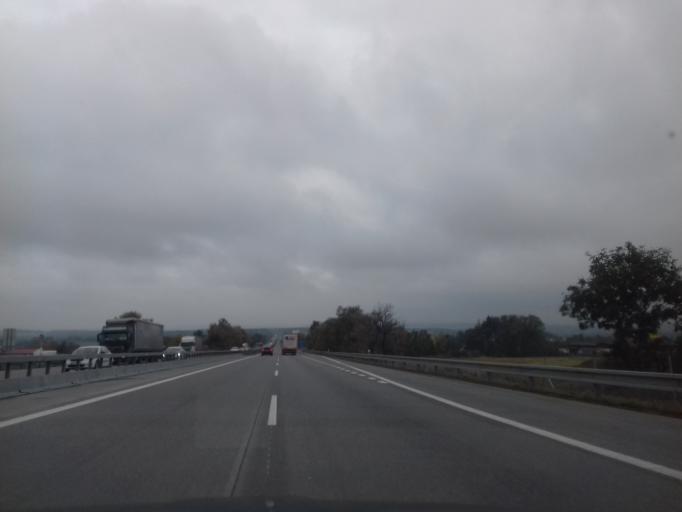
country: CZ
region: Central Bohemia
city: Cechtice
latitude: 49.6540
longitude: 15.1228
